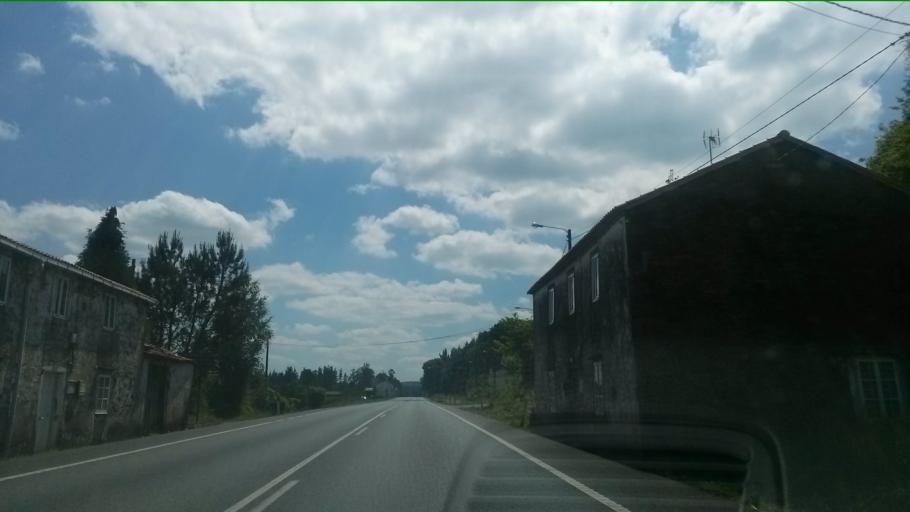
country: ES
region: Galicia
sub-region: Provincia da Coruna
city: Touro
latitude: 42.9572
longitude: -8.3212
